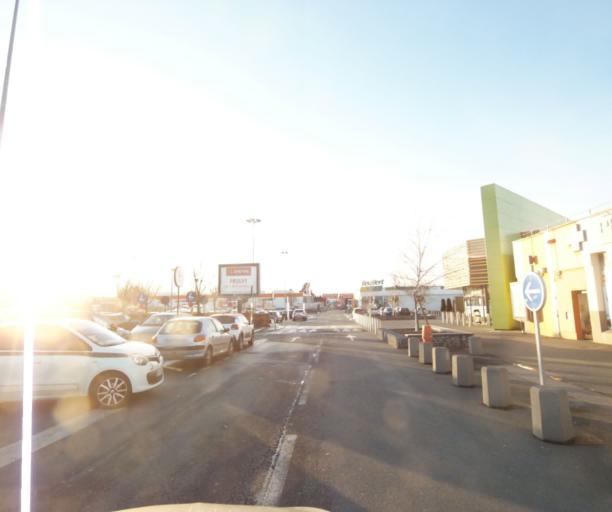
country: FR
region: Nord-Pas-de-Calais
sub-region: Departement du Nord
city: Aulnoy-lez-Valenciennes
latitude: 50.3352
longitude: 3.5173
